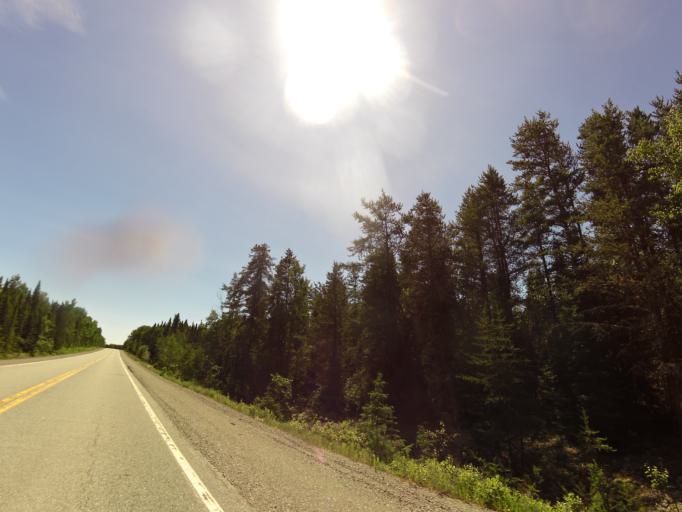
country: CA
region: Quebec
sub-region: Nord-du-Quebec
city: Lebel-sur-Quevillon
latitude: 48.8237
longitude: -77.1219
